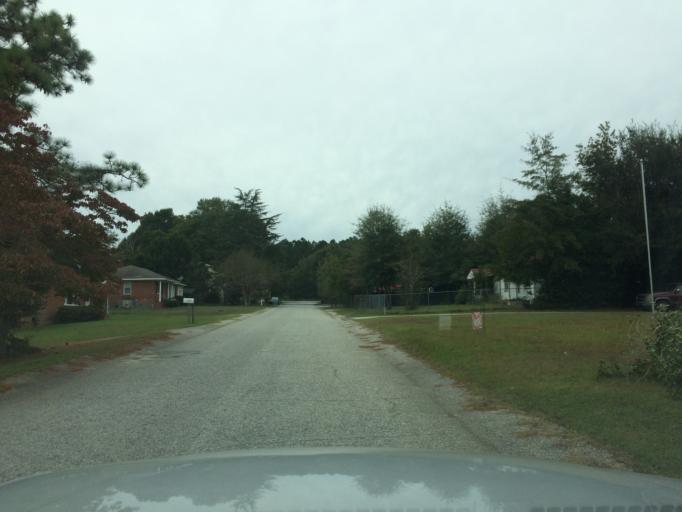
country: US
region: South Carolina
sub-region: Aiken County
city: New Ellenton
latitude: 33.4284
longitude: -81.6860
